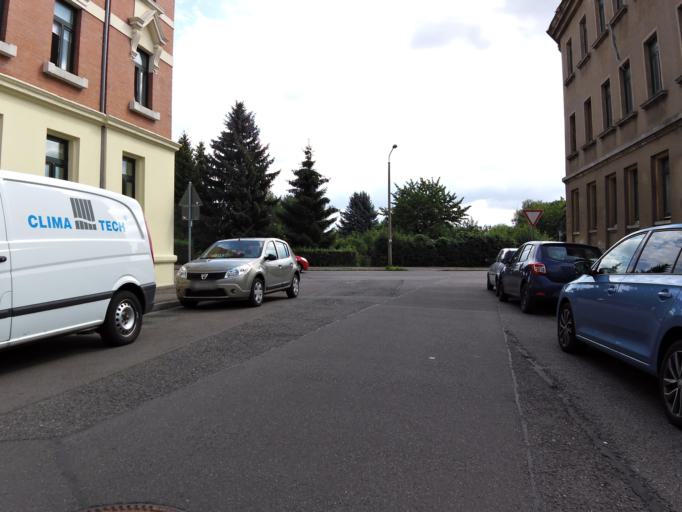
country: DE
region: Saxony
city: Taucha
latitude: 51.3811
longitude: 12.4203
